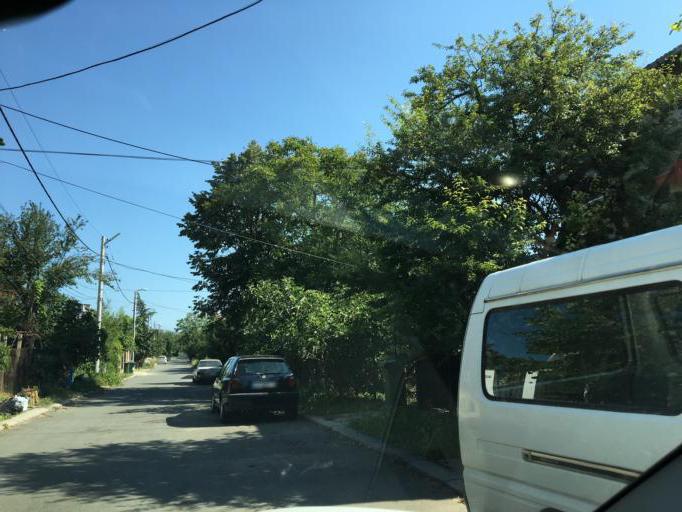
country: BG
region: Burgas
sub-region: Obshtina Kameno
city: Kameno
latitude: 42.6094
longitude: 27.3868
